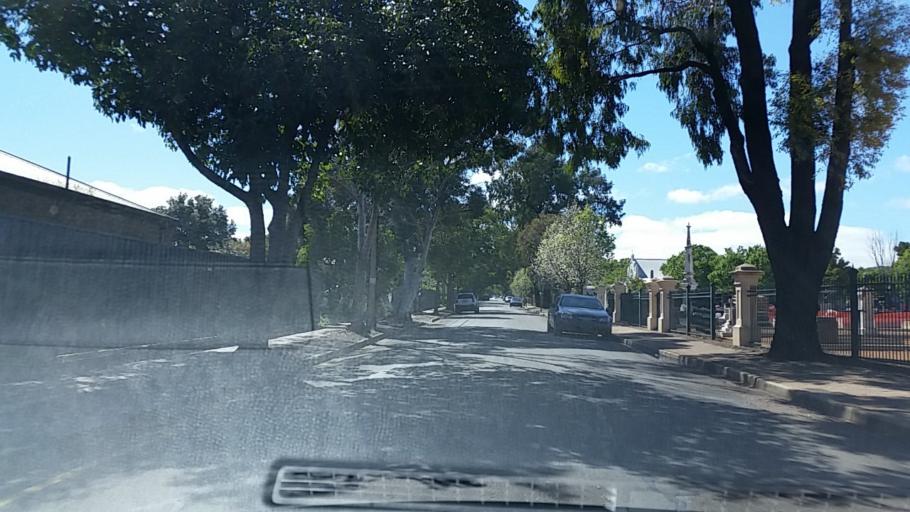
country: AU
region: South Australia
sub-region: Norwood Payneham St Peters
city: Payneham
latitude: -34.9017
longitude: 138.6426
